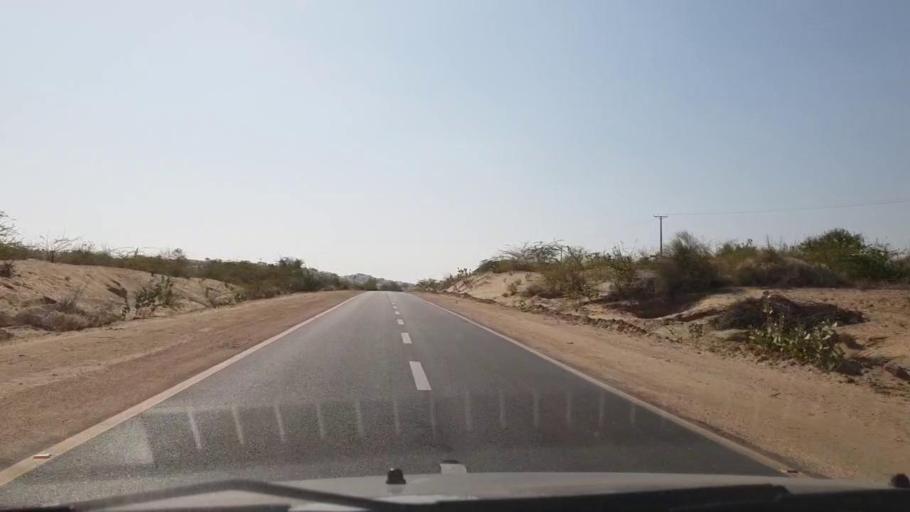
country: PK
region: Sindh
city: Diplo
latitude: 24.4984
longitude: 69.6044
